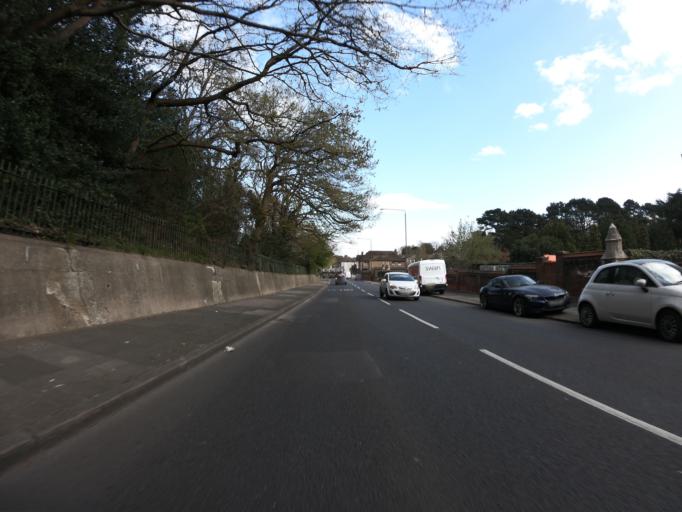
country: GB
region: England
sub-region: Greater London
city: Abbey Wood
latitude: 51.4793
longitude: 0.0989
